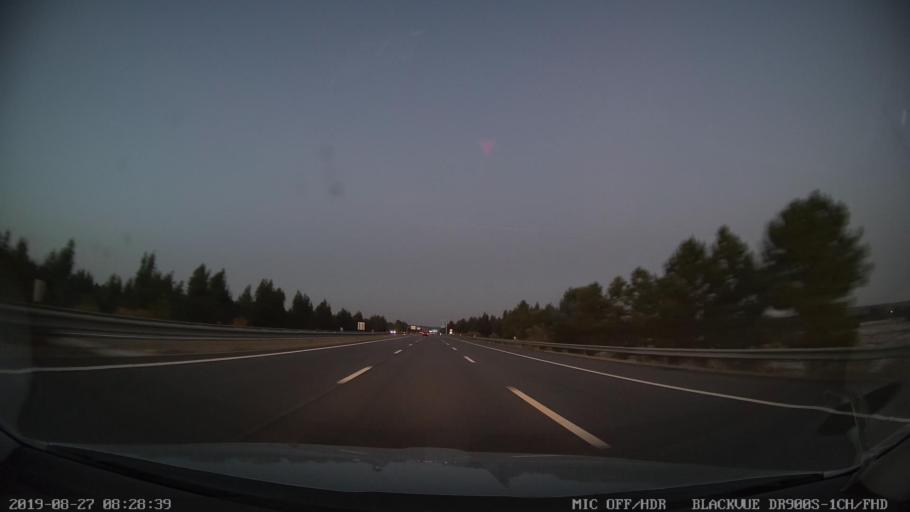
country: PT
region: Evora
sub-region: Vendas Novas
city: Vendas Novas
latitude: 38.6006
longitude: -8.6705
